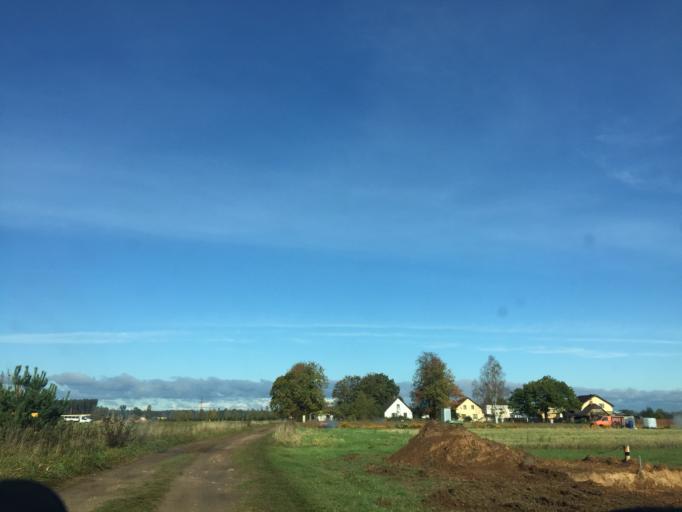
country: LV
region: Adazi
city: Adazi
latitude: 57.0880
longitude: 24.3067
